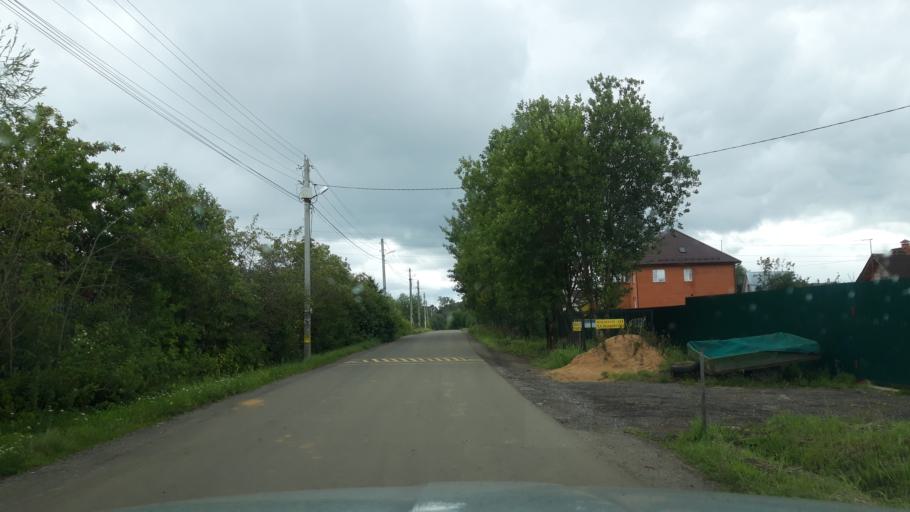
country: RU
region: Moskovskaya
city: Peshki
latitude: 56.0999
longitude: 37.0657
